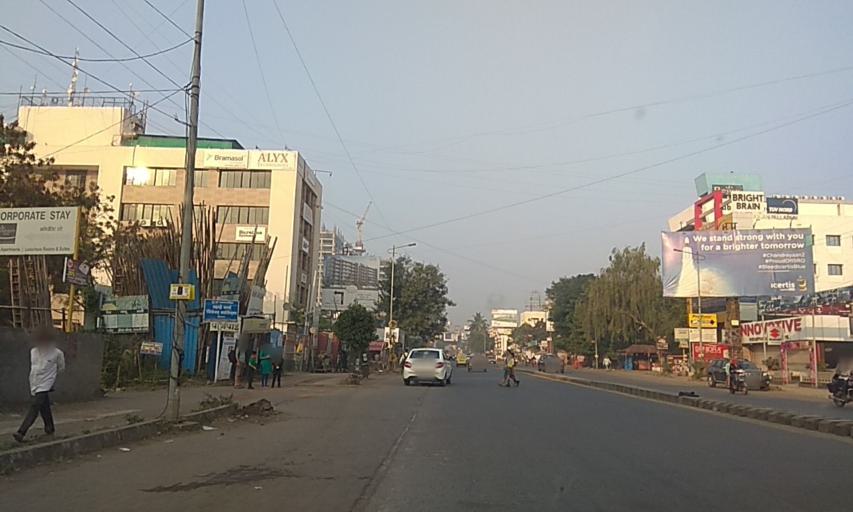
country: IN
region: Maharashtra
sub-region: Pune Division
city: Pimpri
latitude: 18.5641
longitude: 73.7799
